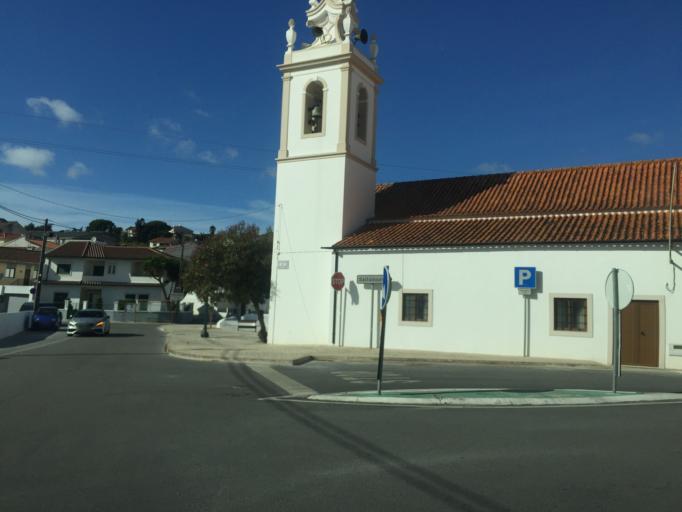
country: PT
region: Coimbra
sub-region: Figueira da Foz
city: Tavarede
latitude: 40.1662
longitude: -8.8443
